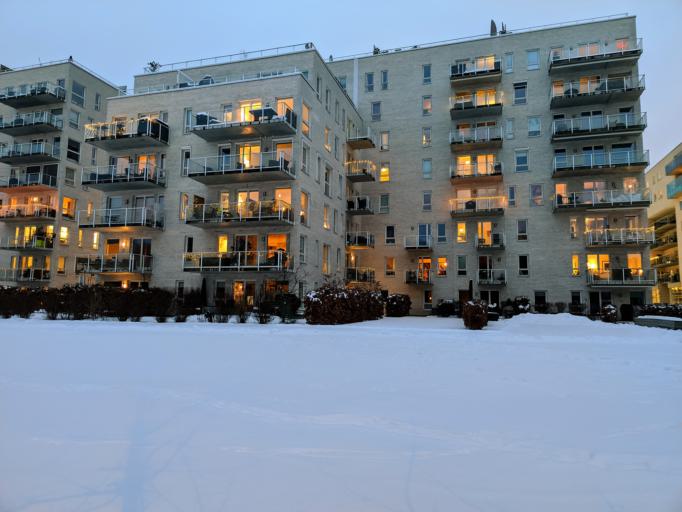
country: NO
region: Oslo
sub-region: Oslo
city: Oslo
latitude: 59.9453
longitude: 10.7659
